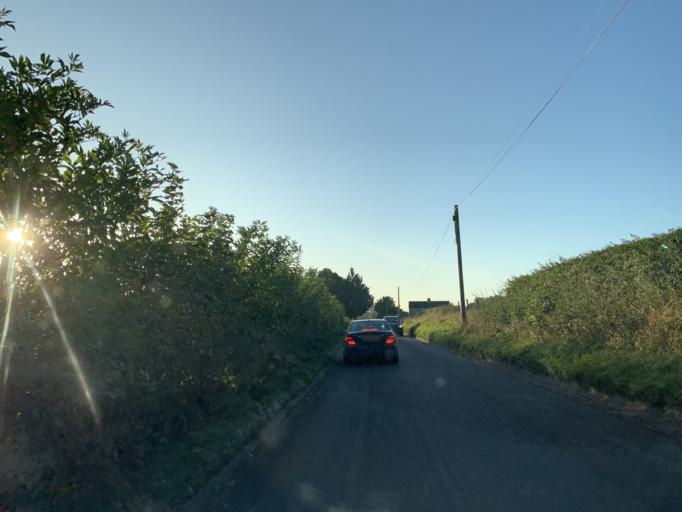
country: GB
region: England
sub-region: Wiltshire
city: Woodford
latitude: 51.1021
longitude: -1.8260
